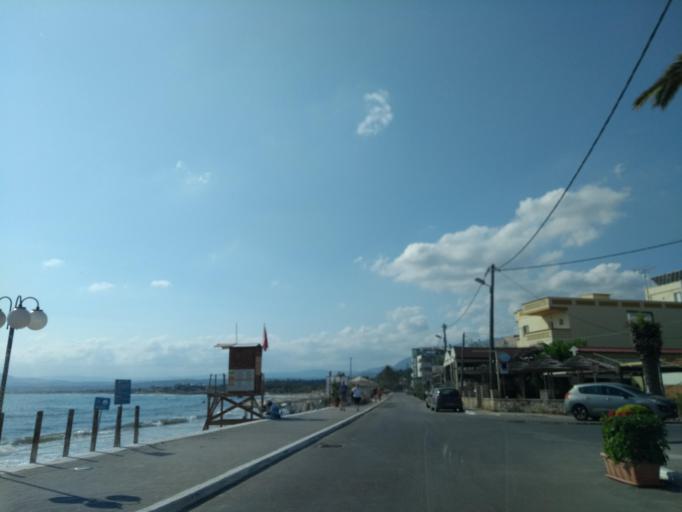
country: GR
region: Crete
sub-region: Nomos Chanias
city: Georgioupolis
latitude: 35.3624
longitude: 24.2627
